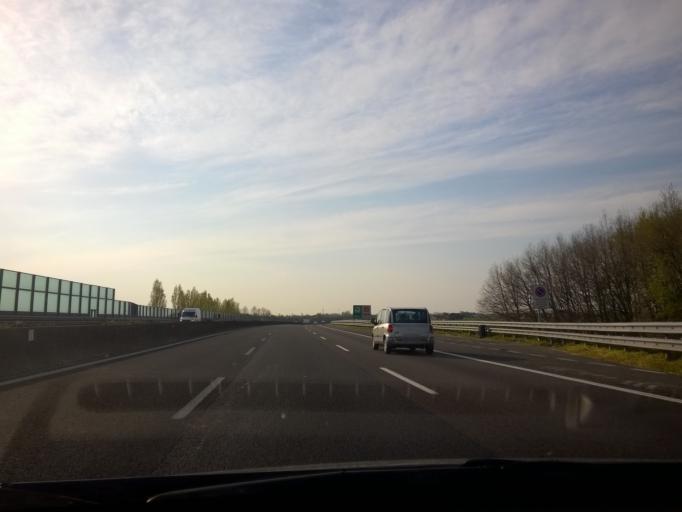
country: IT
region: Emilia-Romagna
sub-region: Forli-Cesena
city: Santa Maria Nuova
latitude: 44.2080
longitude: 12.1926
